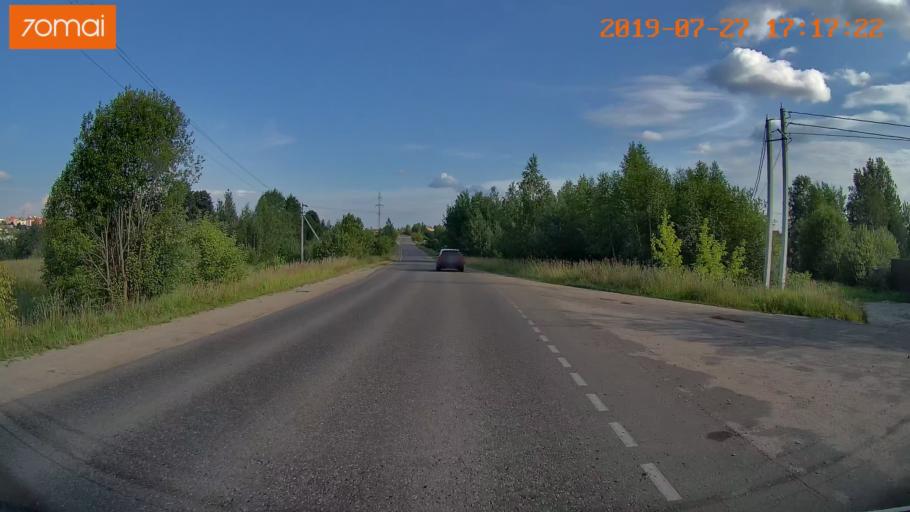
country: RU
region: Ivanovo
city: Novo-Talitsy
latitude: 57.0378
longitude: 40.8939
